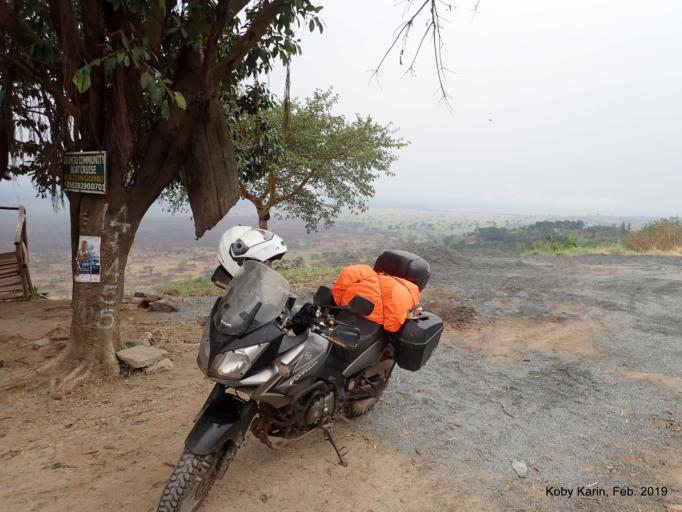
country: UG
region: Western Region
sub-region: Rubirizi District
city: Rubirizi
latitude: -0.2251
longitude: 30.0942
